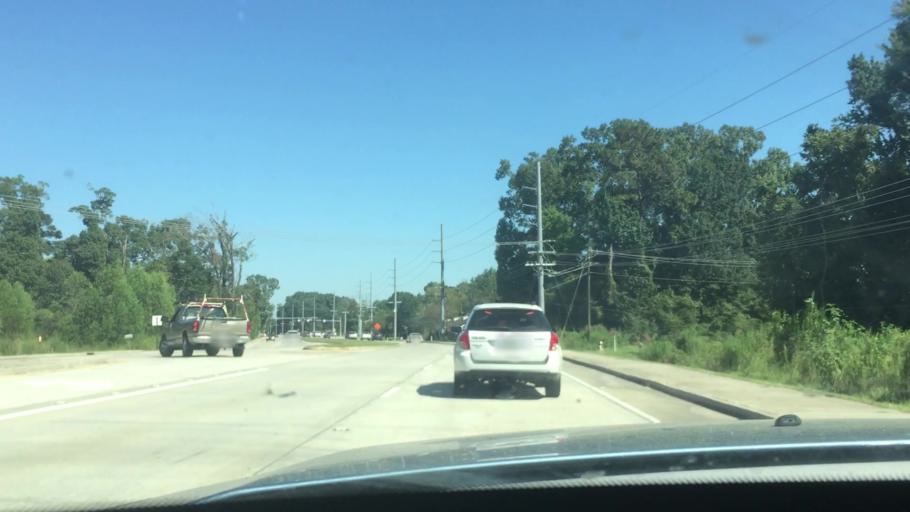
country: US
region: Louisiana
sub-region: East Baton Rouge Parish
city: Shenandoah
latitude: 30.4260
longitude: -91.0112
